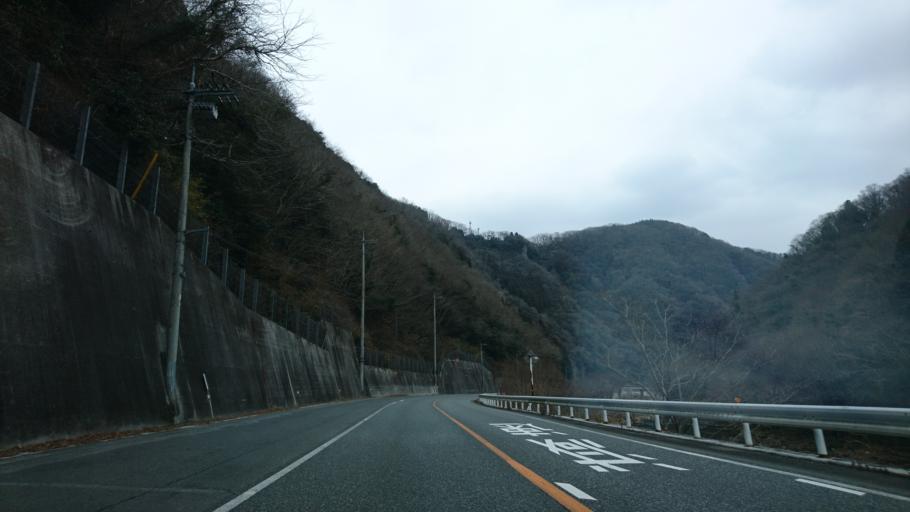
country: JP
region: Okayama
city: Niimi
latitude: 34.9122
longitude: 133.5237
